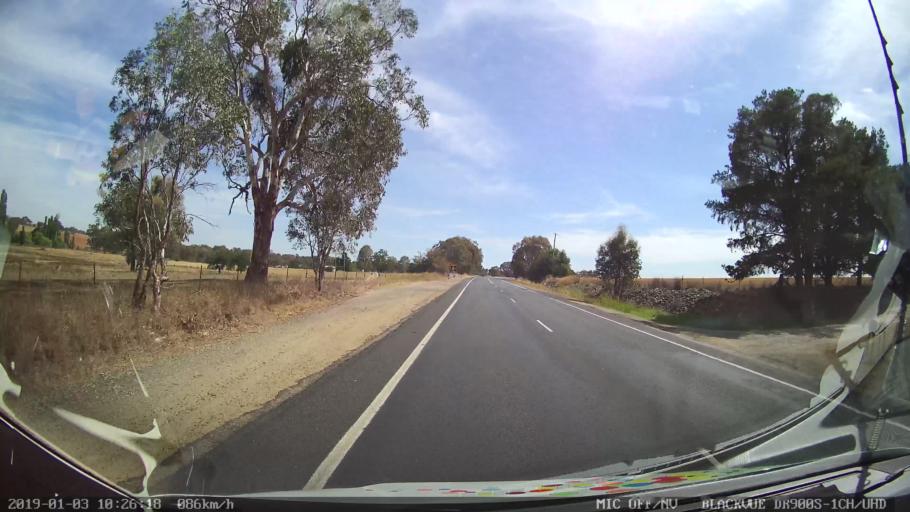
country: AU
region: New South Wales
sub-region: Young
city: Young
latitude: -34.4143
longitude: 148.2485
